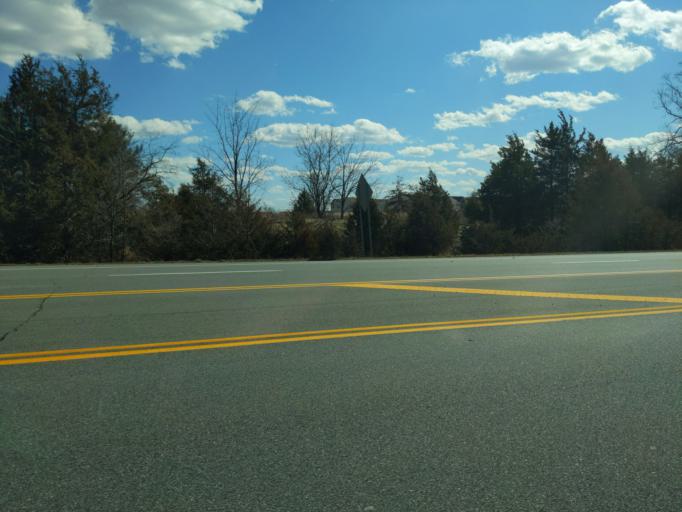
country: US
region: Pennsylvania
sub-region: Montgomery County
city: East Greenville
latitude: 40.4037
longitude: -75.4907
